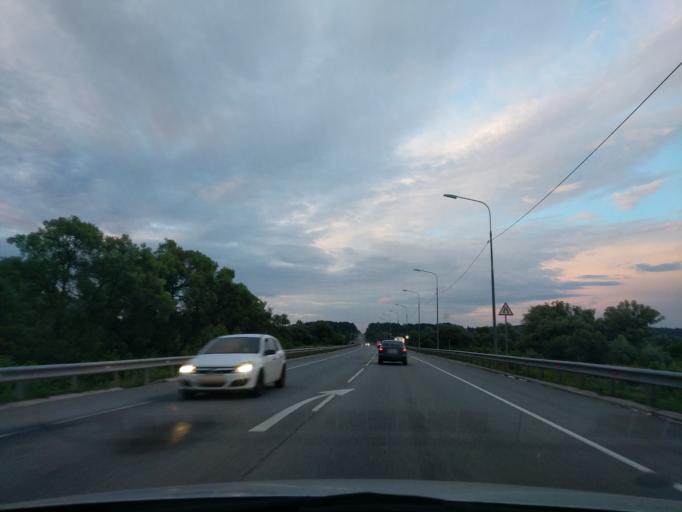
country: RU
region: Kaluga
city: Obninsk
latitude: 55.0575
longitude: 36.5796
